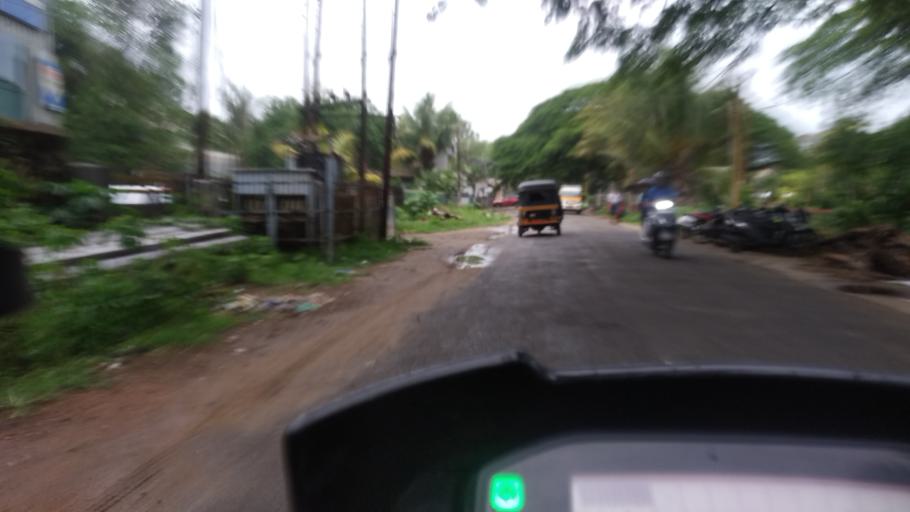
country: IN
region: Kerala
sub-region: Alappuzha
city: Alleppey
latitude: 9.5001
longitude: 76.3222
